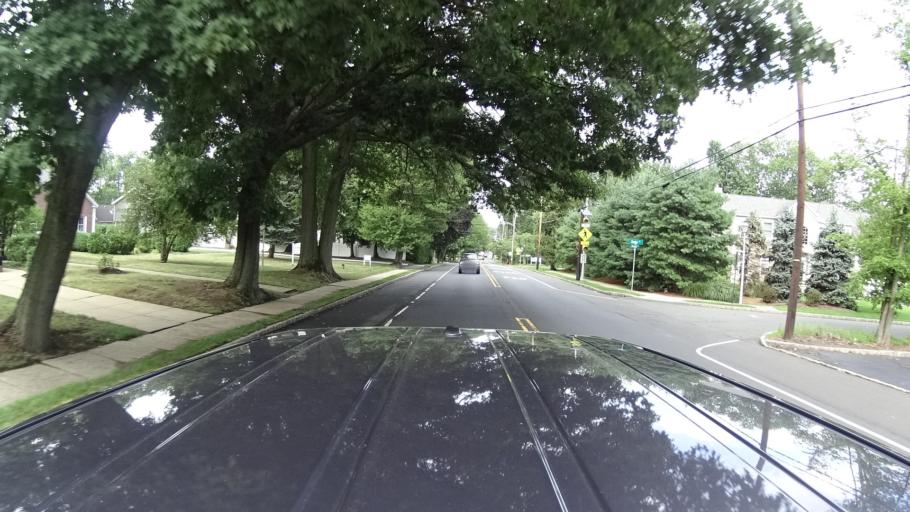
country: US
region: New Jersey
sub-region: Union County
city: New Providence
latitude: 40.7034
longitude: -74.4120
